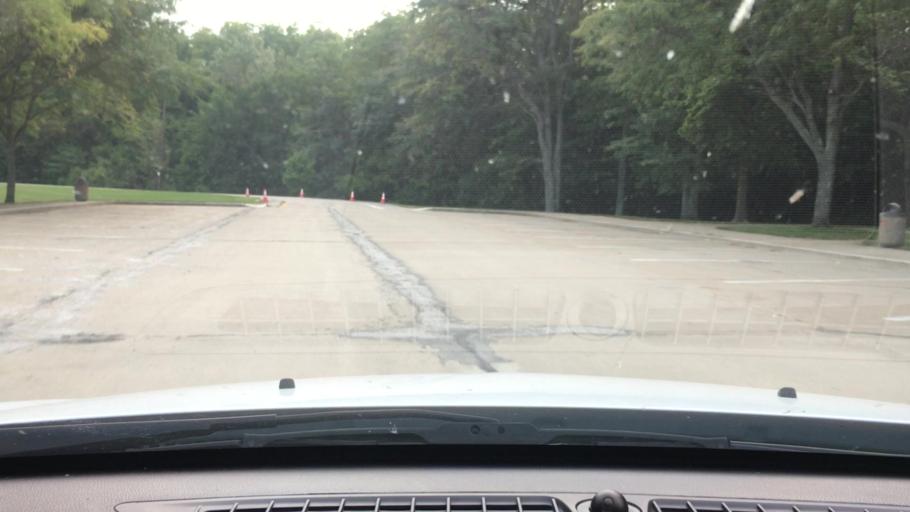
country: US
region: Illinois
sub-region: McLean County
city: Twin Grove
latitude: 40.3587
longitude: -89.1100
